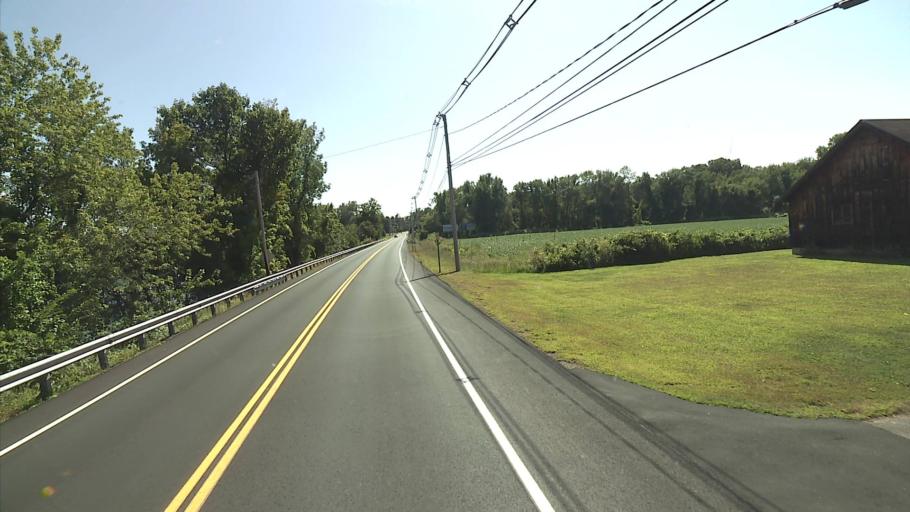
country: US
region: Connecticut
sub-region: Hartford County
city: Windsor Locks
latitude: 41.9068
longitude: -72.6249
